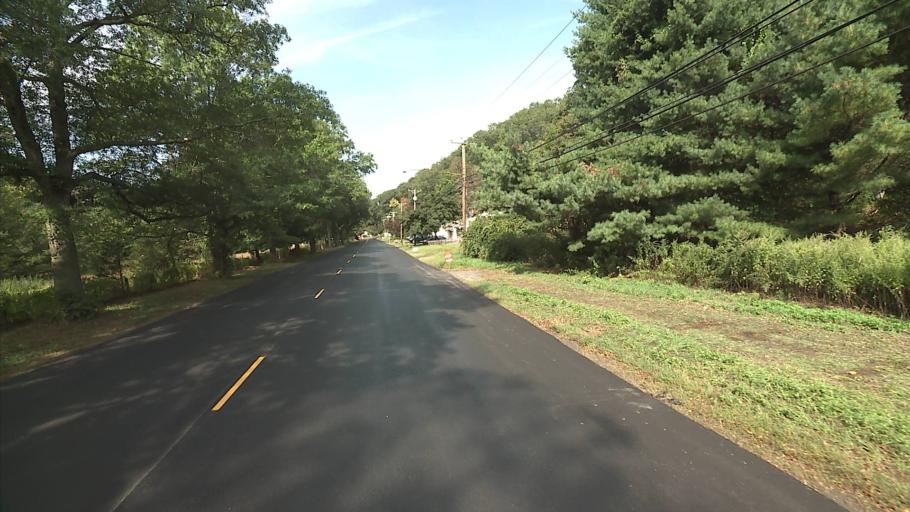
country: US
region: Connecticut
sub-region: Fairfield County
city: Shelton
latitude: 41.3512
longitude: -73.1319
